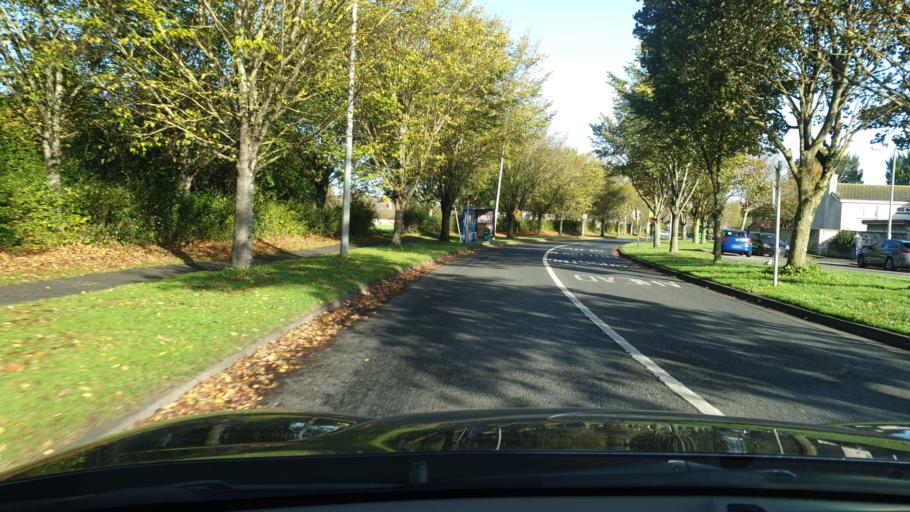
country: IE
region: Leinster
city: Lucan
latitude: 53.3469
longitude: -6.4432
